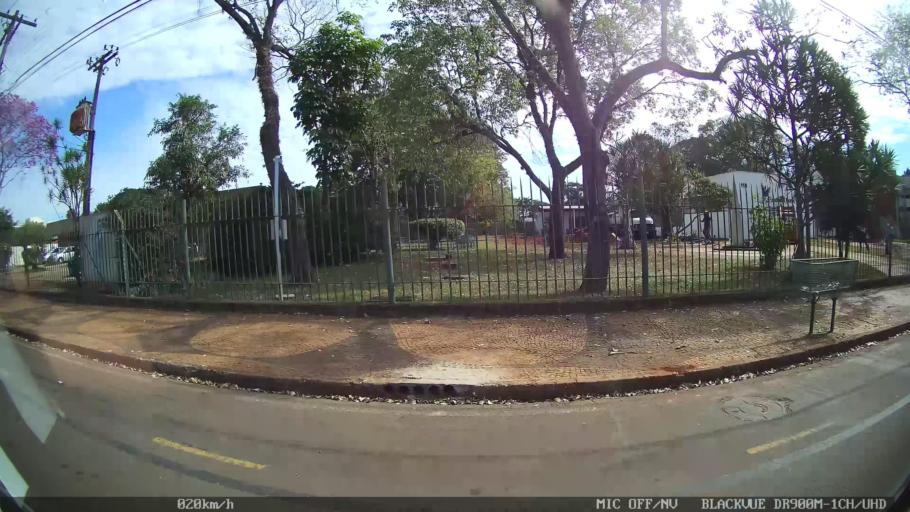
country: BR
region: Sao Paulo
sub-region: Santa Barbara D'Oeste
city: Santa Barbara d'Oeste
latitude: -22.7563
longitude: -47.4270
